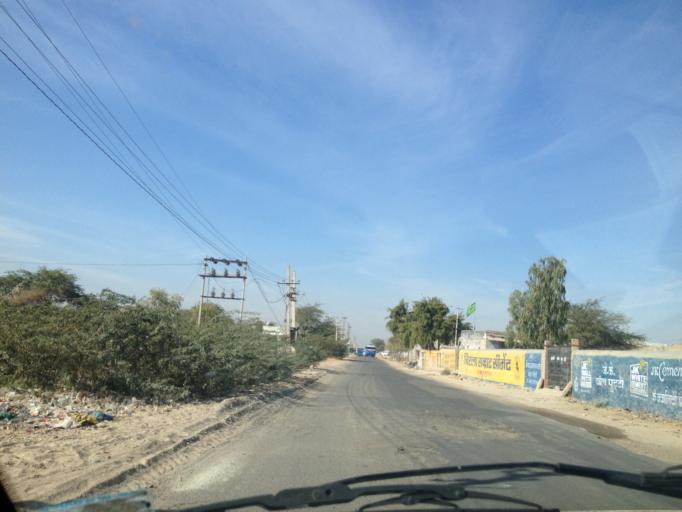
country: IN
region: Rajasthan
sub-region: Nagaur
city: Merta
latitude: 26.6444
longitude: 74.0243
